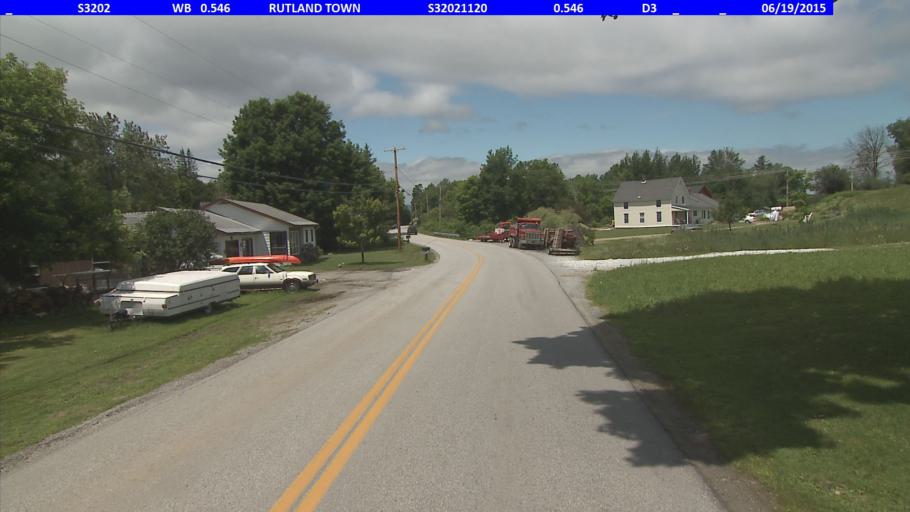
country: US
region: Vermont
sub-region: Rutland County
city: Rutland
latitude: 43.5876
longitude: -72.9588
